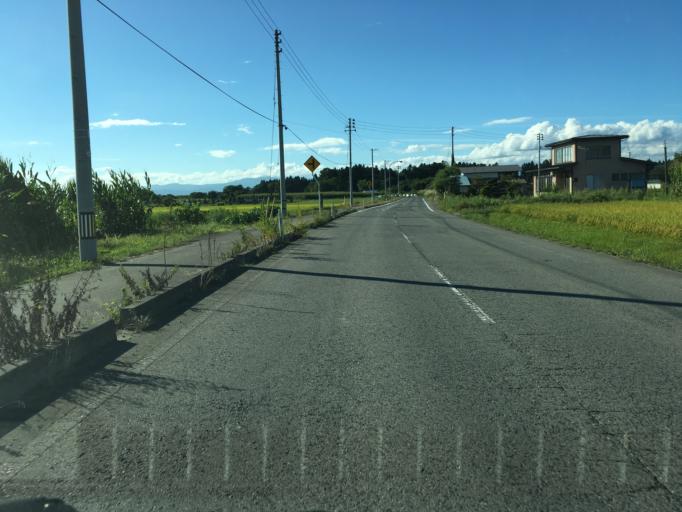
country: JP
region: Yamagata
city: Takahata
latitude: 37.9764
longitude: 140.1576
